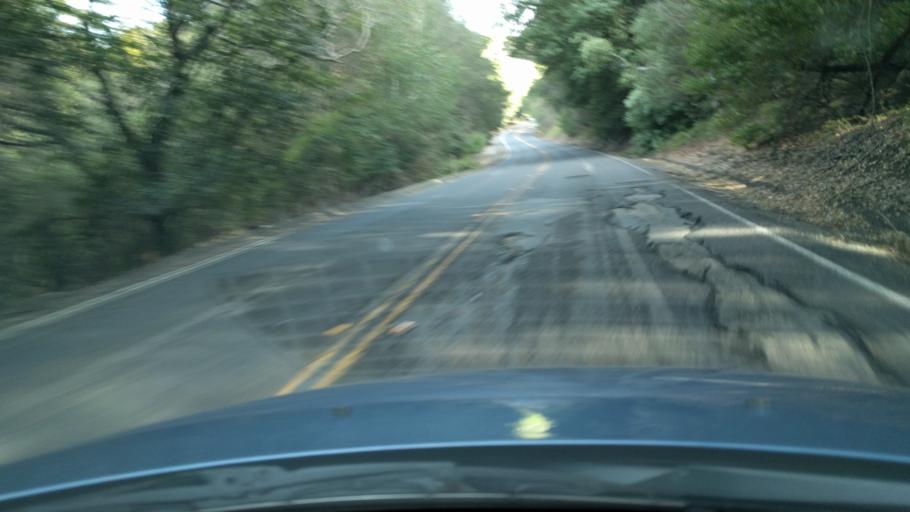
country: US
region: California
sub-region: Contra Costa County
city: San Ramon
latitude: 37.7857
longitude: -122.0037
